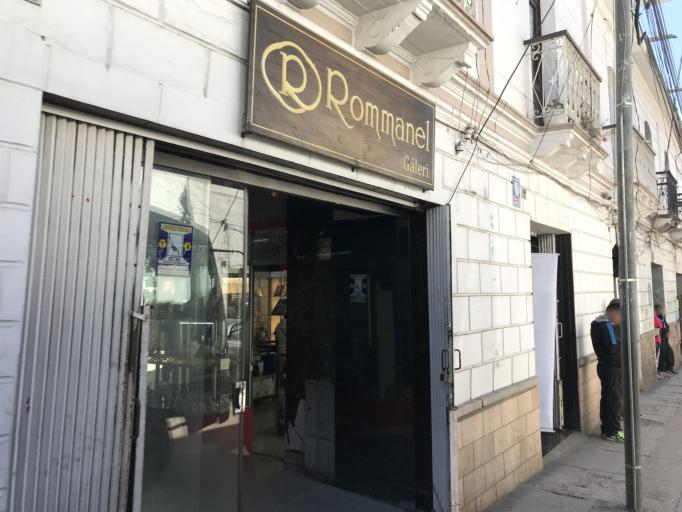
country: BO
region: Chuquisaca
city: Sucre
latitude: -19.0430
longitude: -65.2578
